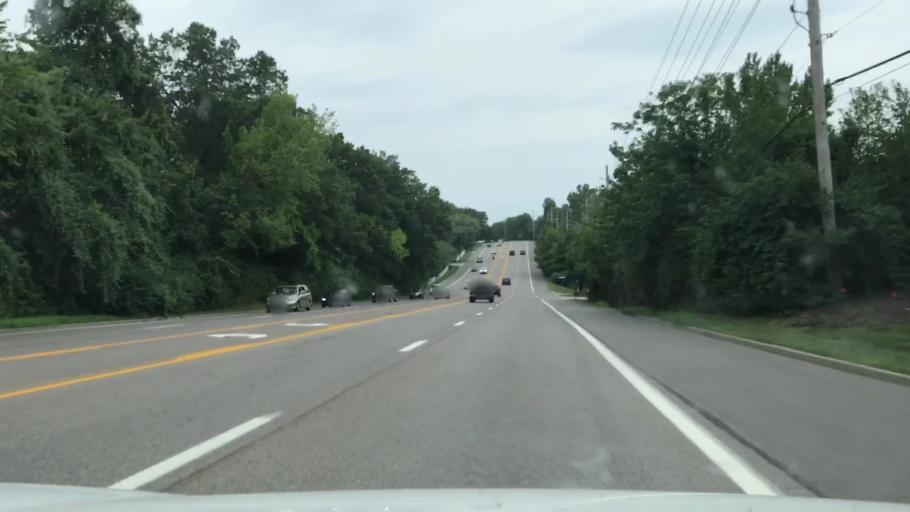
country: US
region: Missouri
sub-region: Saint Louis County
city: Clarkson Valley
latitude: 38.6197
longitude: -90.5832
